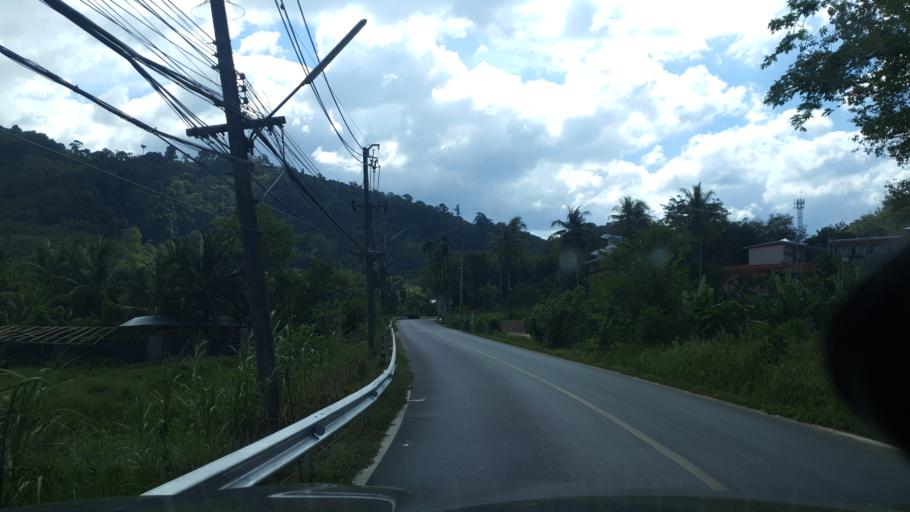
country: TH
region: Phuket
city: Thalang
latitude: 8.0691
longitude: 98.2939
